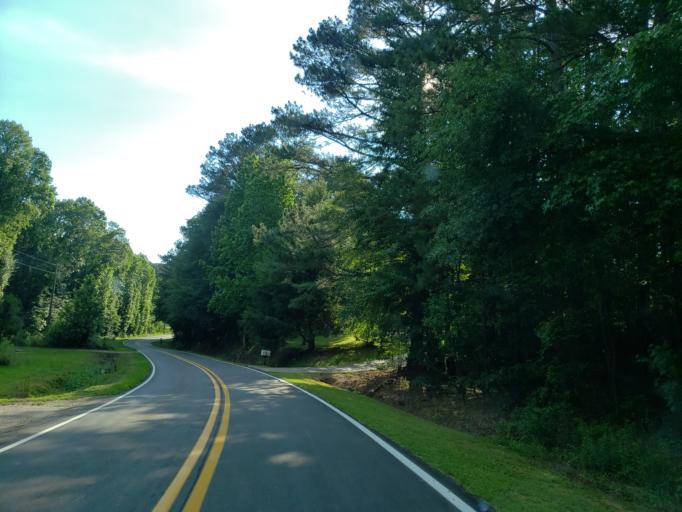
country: US
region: Georgia
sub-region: Haralson County
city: Buchanan
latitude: 33.8560
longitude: -85.2068
